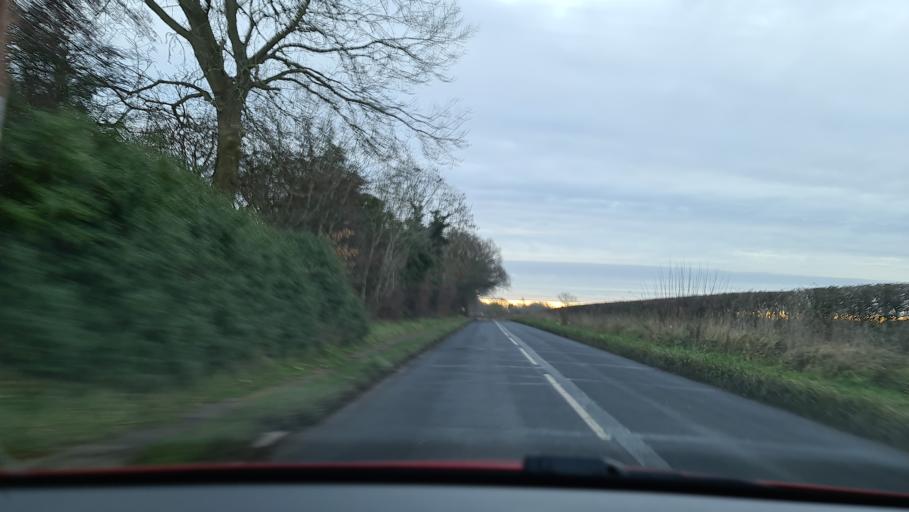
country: GB
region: England
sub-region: Buckinghamshire
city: Amersham
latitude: 51.6894
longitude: -0.6301
